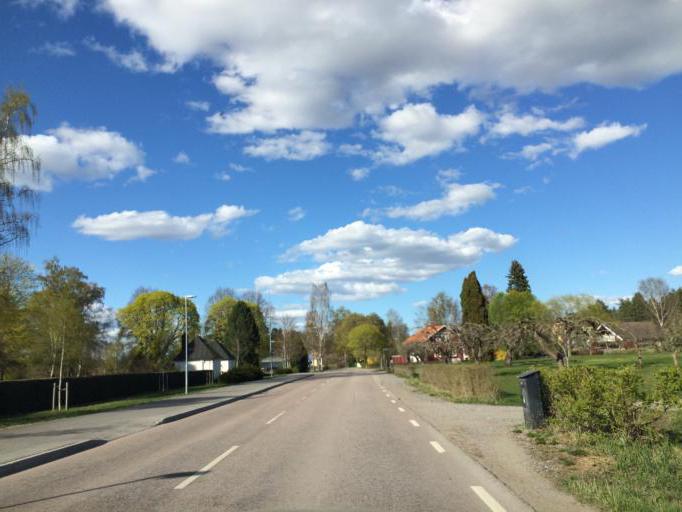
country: SE
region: Soedermanland
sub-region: Eskilstuna Kommun
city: Hallbybrunn
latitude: 59.3688
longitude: 16.4413
